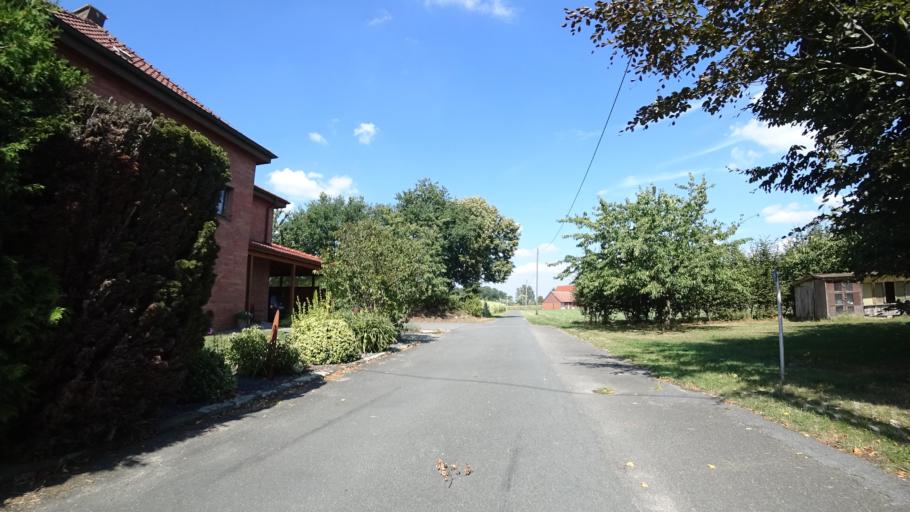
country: DE
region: North Rhine-Westphalia
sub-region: Regierungsbezirk Detmold
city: Rheda-Wiedenbruck
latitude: 51.8869
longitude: 8.2763
